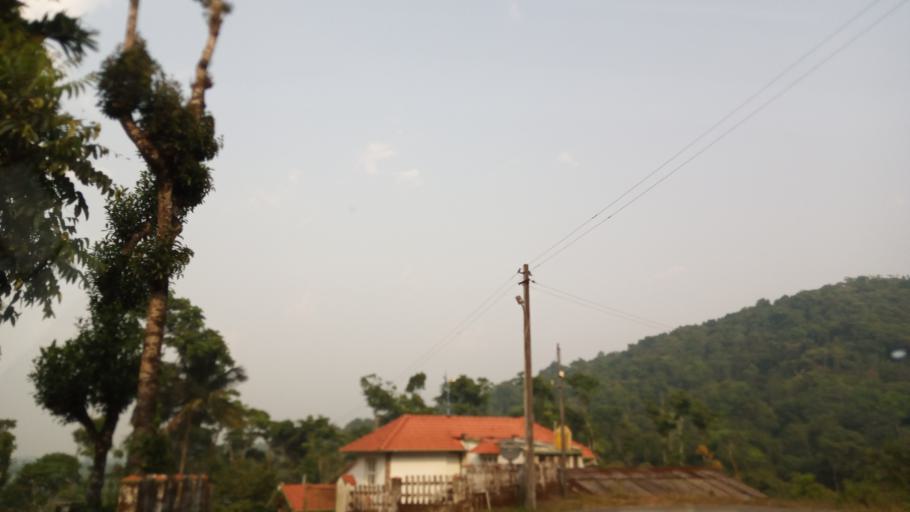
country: IN
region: Karnataka
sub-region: Chikmagalur
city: Mudigere
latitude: 13.0145
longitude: 75.6285
